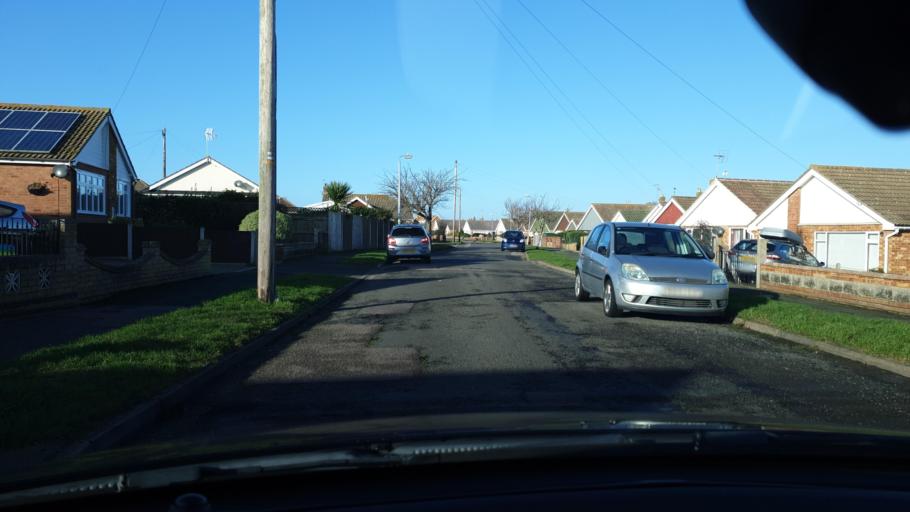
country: GB
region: England
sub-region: Essex
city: Clacton-on-Sea
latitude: 51.8084
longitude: 1.1985
